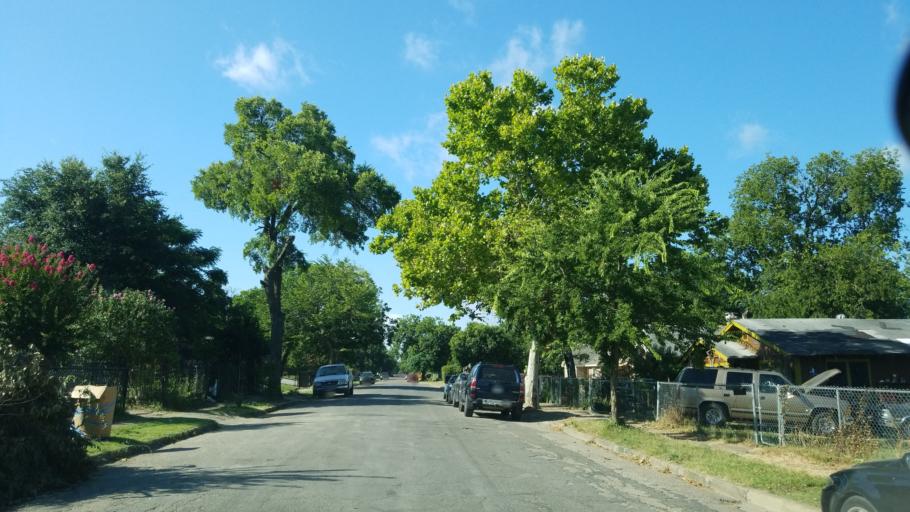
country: US
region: Texas
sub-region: Dallas County
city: Dallas
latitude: 32.7177
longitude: -96.8071
